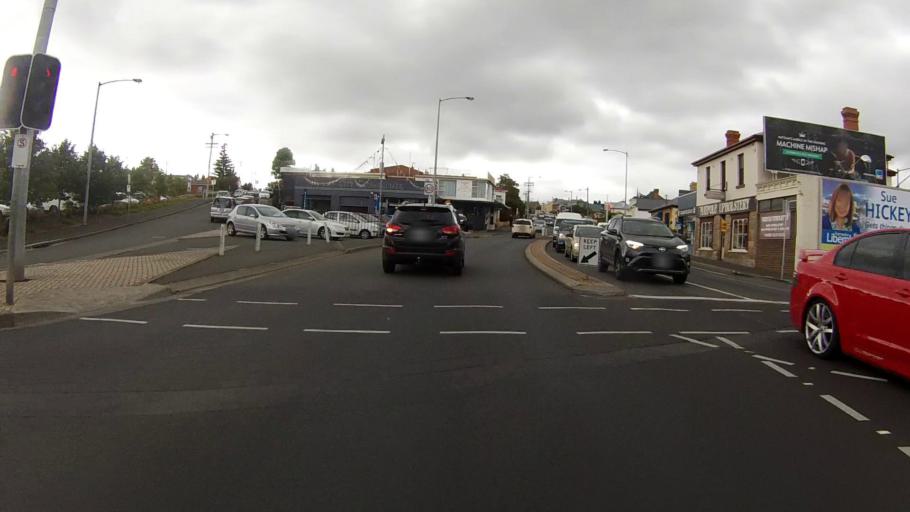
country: AU
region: Tasmania
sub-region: Hobart
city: New Town
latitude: -42.8558
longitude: 147.3035
